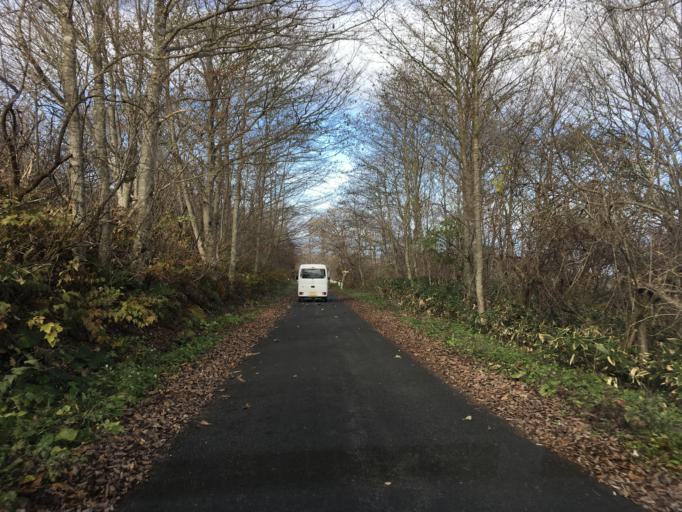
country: JP
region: Iwate
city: Mizusawa
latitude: 39.1328
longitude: 141.3066
